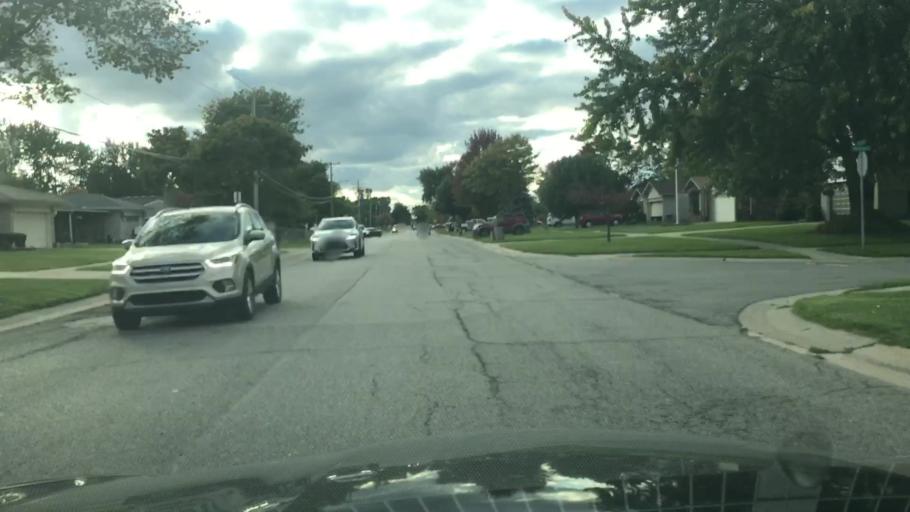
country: US
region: Michigan
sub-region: Macomb County
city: Sterling Heights
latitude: 42.5722
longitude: -83.0577
